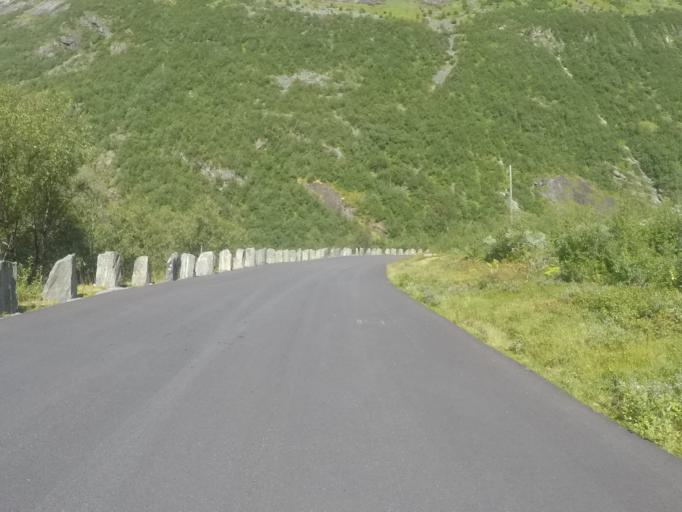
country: NO
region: More og Romsdal
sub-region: Norddal
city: Valldal
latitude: 61.9384
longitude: 7.2689
